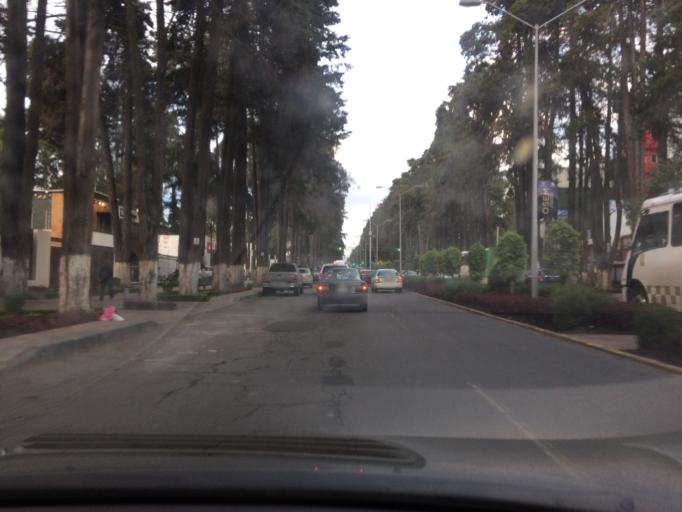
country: MX
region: Mexico
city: Toluca
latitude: 19.2771
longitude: -99.6591
